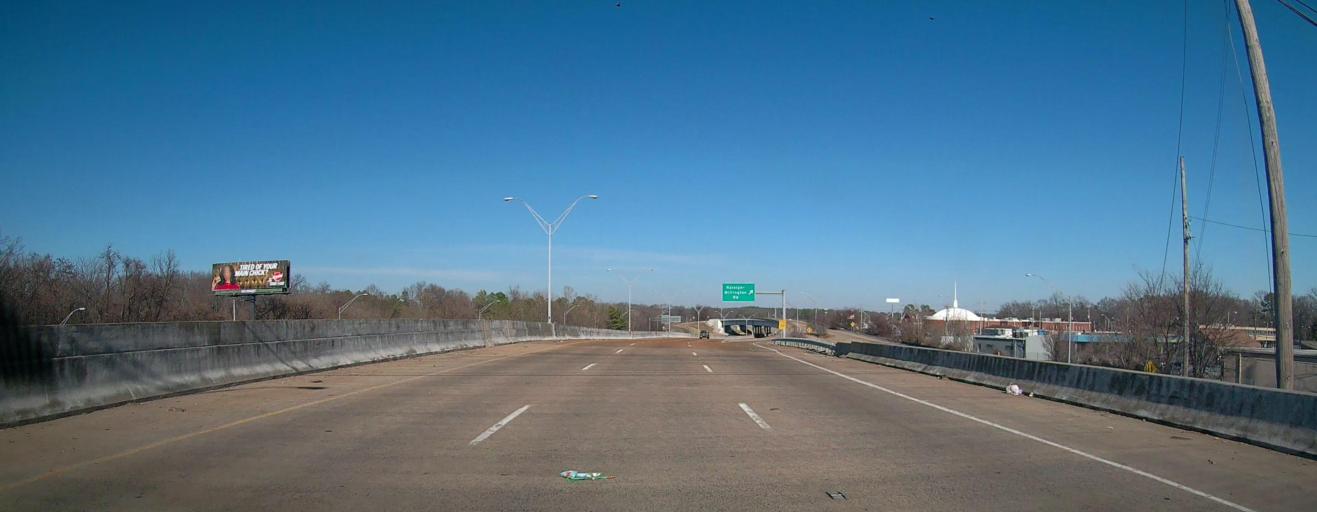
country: US
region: Tennessee
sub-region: Shelby County
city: Bartlett
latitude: 35.2053
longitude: -89.9234
